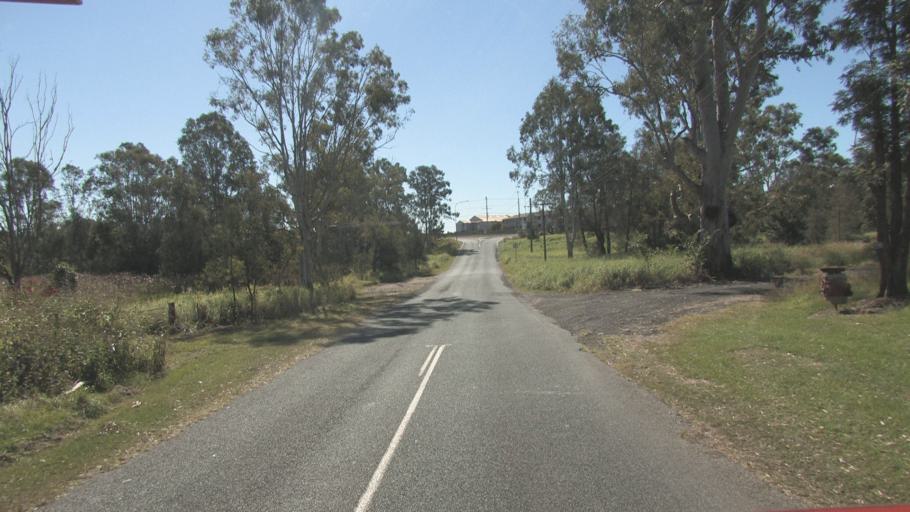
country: AU
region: Queensland
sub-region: Logan
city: Waterford West
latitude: -27.6959
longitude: 153.1485
